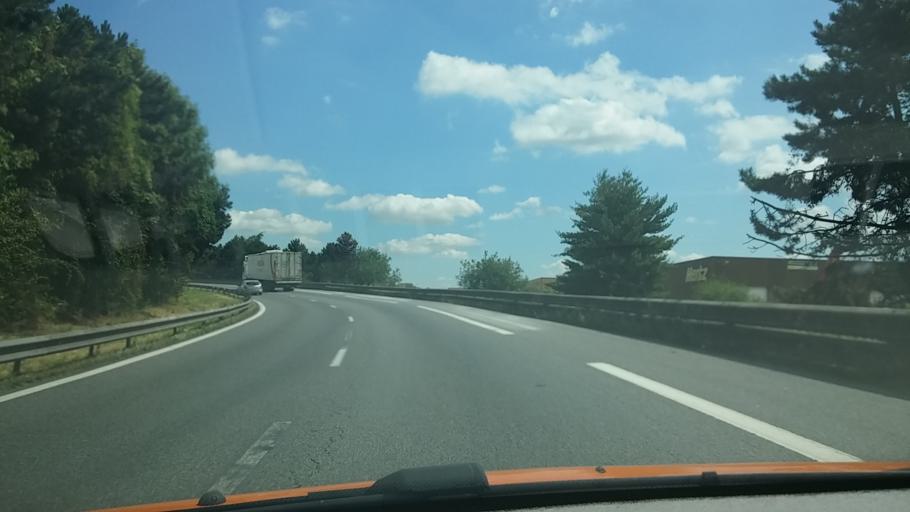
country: FR
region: Ile-de-France
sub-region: Departement de Seine-et-Marne
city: Croissy-Beaubourg
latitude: 48.8303
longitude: 2.6674
